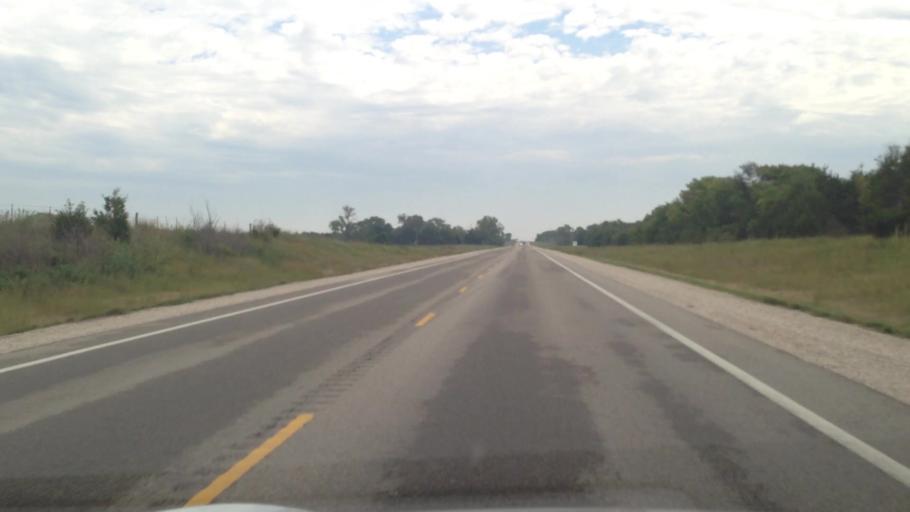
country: US
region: Kansas
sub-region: Allen County
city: Iola
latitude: 37.9104
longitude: -95.1226
